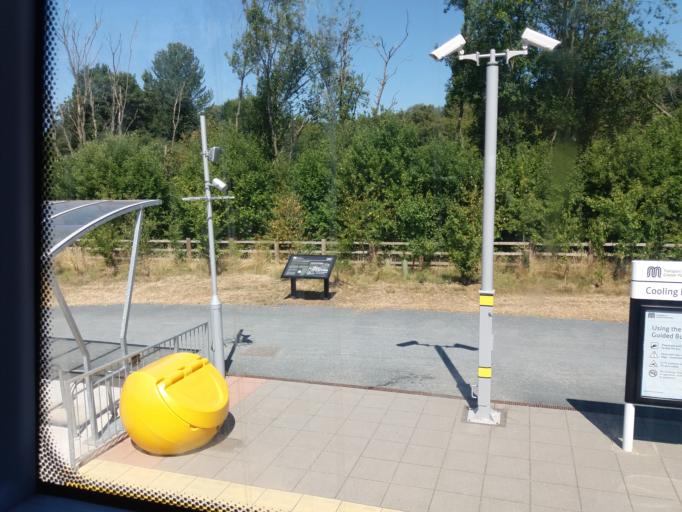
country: GB
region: England
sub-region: Borough of Wigan
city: Tyldesley
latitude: 53.5112
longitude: -2.4787
